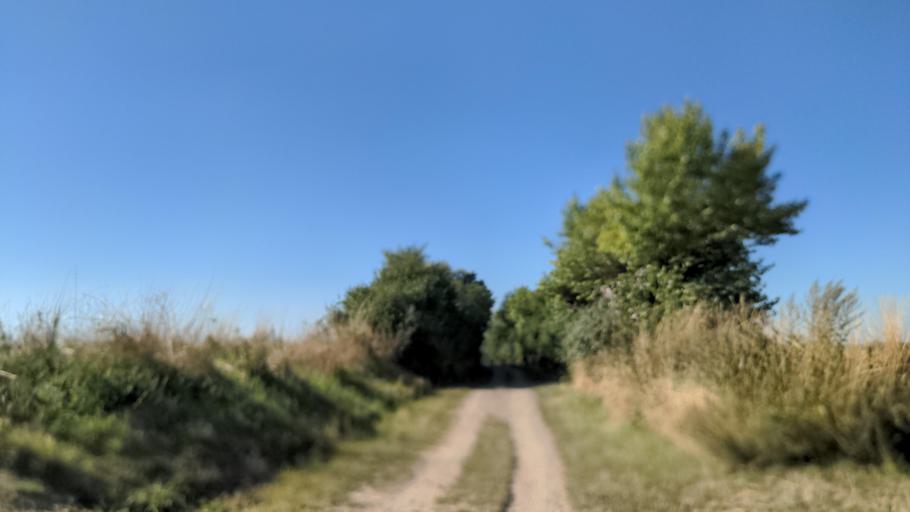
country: DE
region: Mecklenburg-Vorpommern
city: Ostseebad Boltenhagen
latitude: 53.9667
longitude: 11.2354
